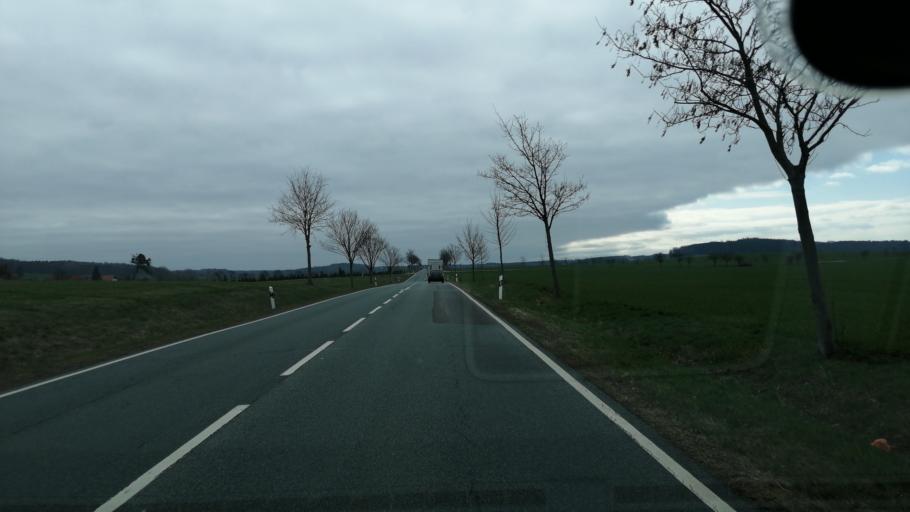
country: DE
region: Saxony
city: Lobau
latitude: 51.0743
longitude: 14.6803
